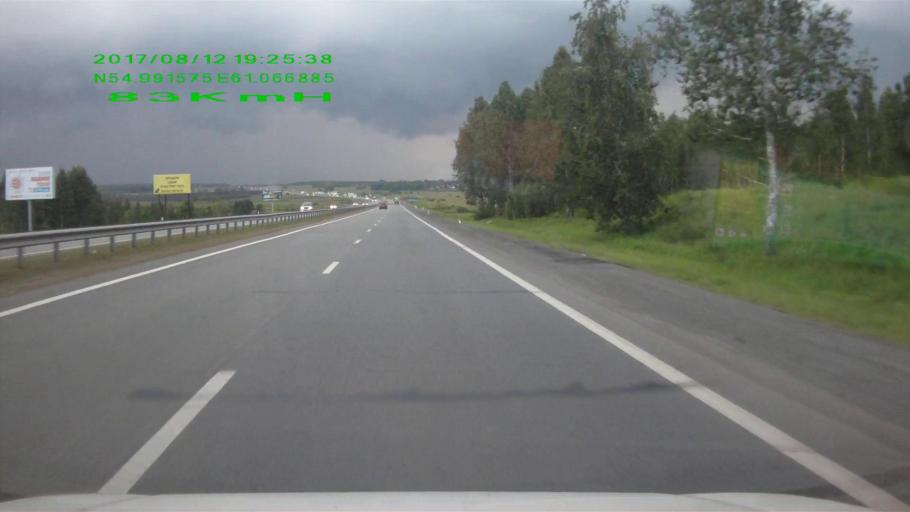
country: RU
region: Chelyabinsk
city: Poletayevo
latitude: 54.9914
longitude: 61.0633
